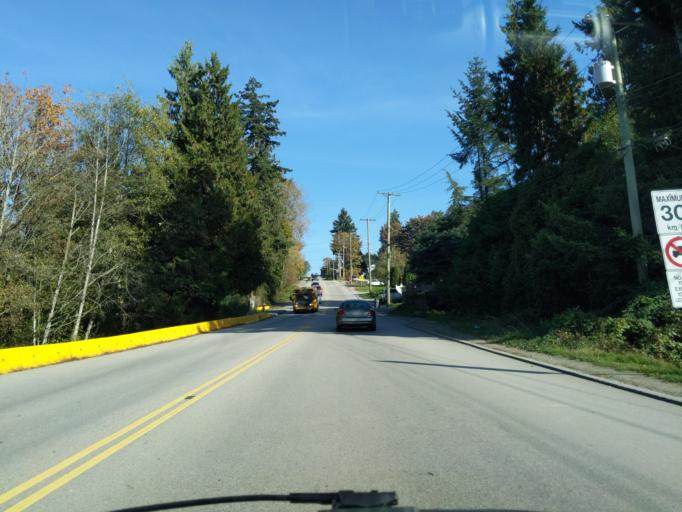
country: CA
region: British Columbia
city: New Westminster
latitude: 49.1918
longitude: -122.8805
